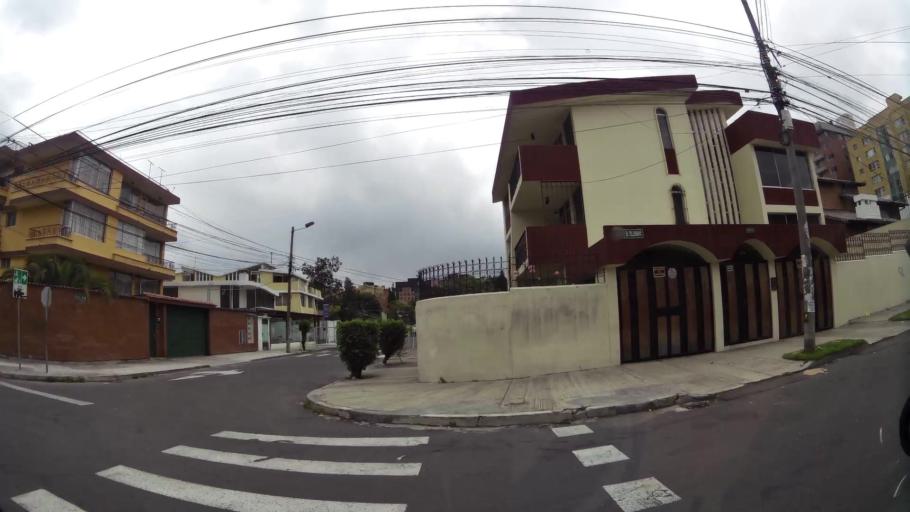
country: EC
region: Pichincha
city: Quito
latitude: -0.1735
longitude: -78.4776
